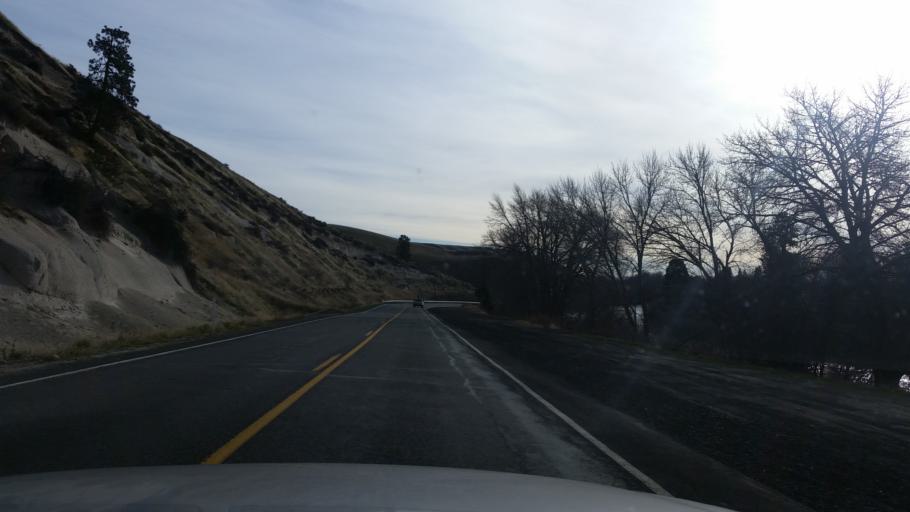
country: US
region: Washington
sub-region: Kittitas County
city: Ellensburg
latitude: 47.1003
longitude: -120.6942
